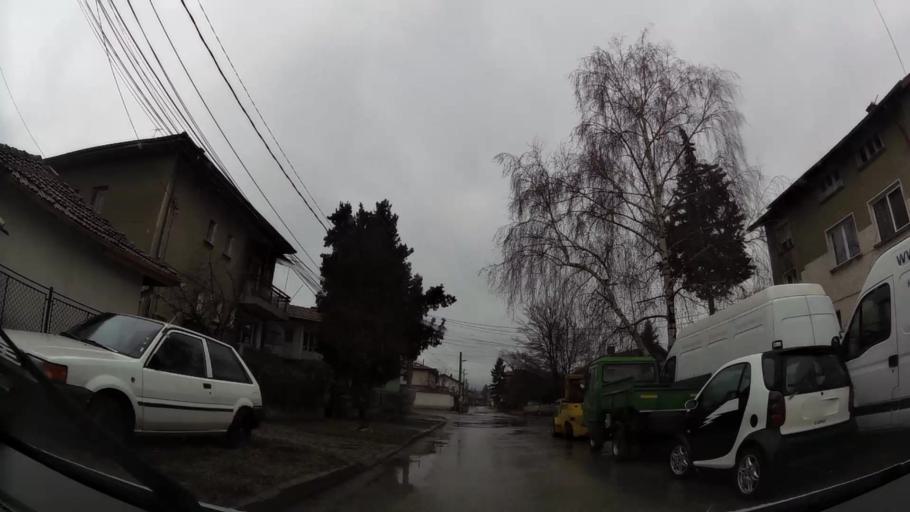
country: BG
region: Sofia-Capital
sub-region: Stolichna Obshtina
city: Sofia
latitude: 42.6274
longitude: 23.4124
